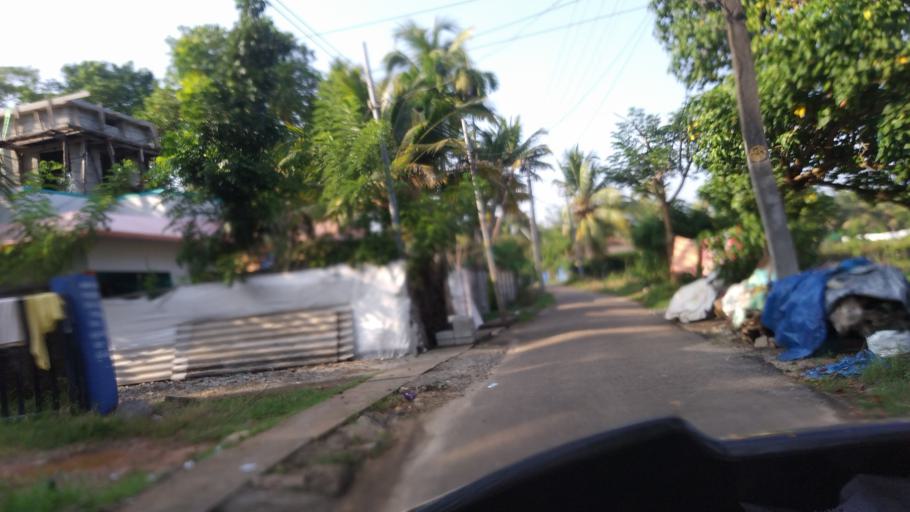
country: IN
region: Kerala
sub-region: Ernakulam
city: Elur
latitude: 10.0454
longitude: 76.2265
